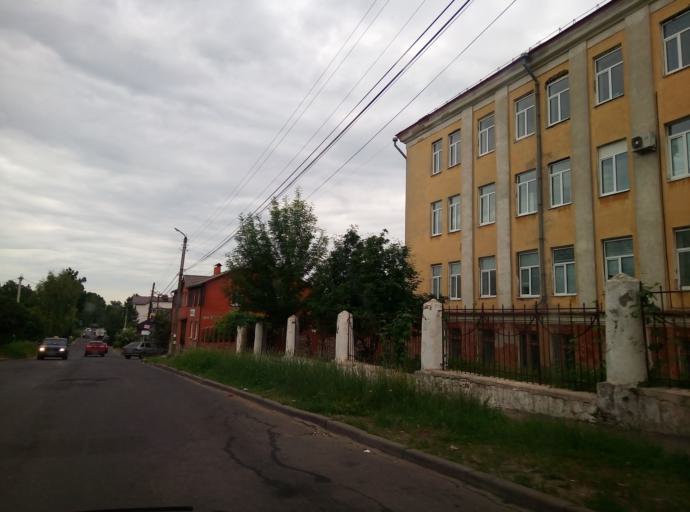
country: RU
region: Kursk
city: Kursk
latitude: 51.7409
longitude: 36.1849
